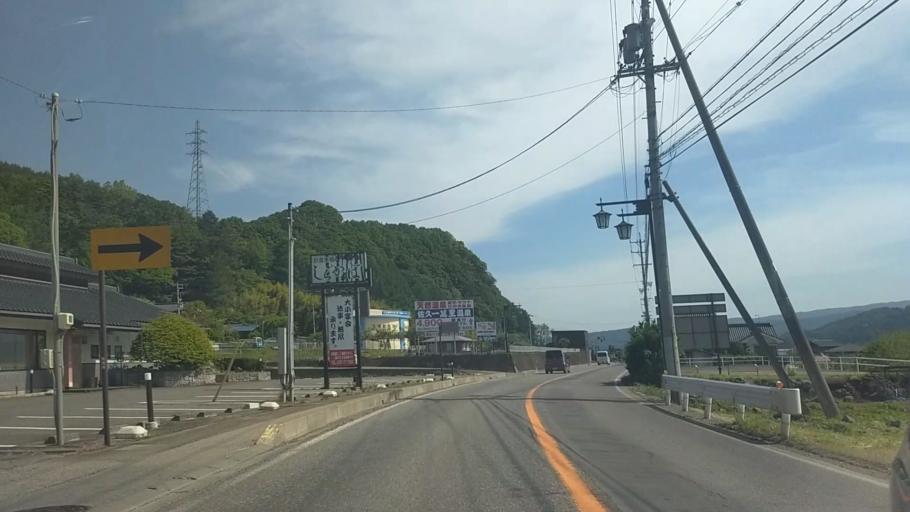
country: JP
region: Nagano
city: Saku
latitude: 36.1529
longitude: 138.4759
